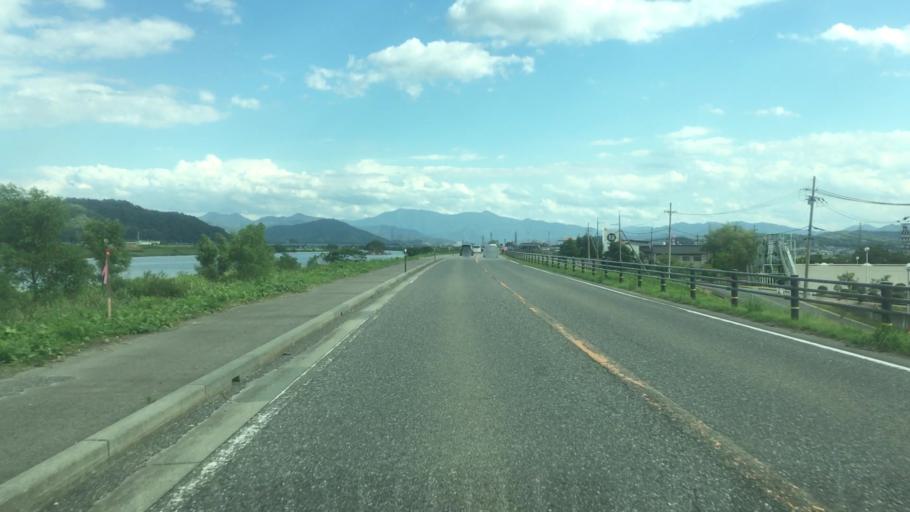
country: JP
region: Hyogo
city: Toyooka
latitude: 35.5714
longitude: 134.8080
